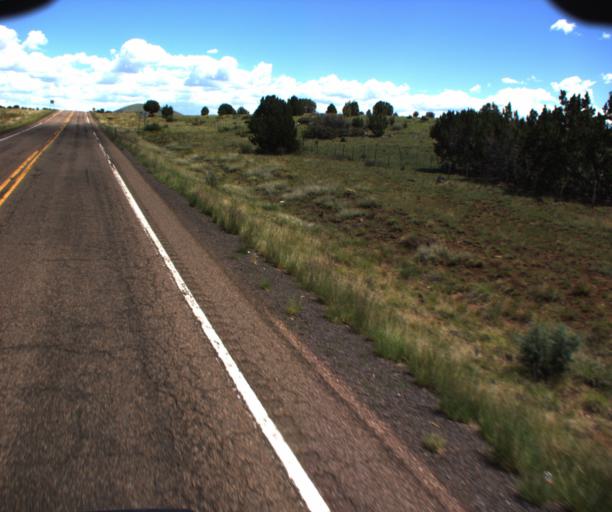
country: US
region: Arizona
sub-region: Apache County
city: Springerville
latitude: 34.2575
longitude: -109.5495
